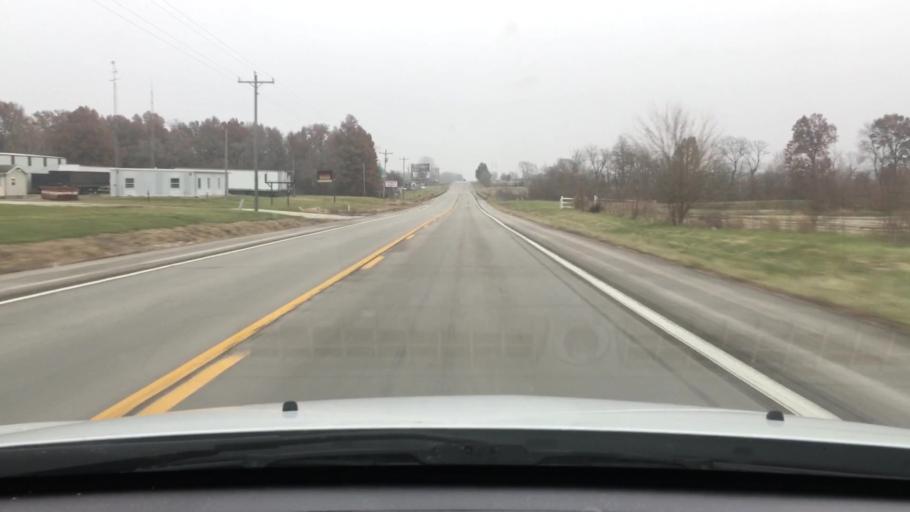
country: US
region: Missouri
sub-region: Audrain County
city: Mexico
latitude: 39.1637
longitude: -91.8101
